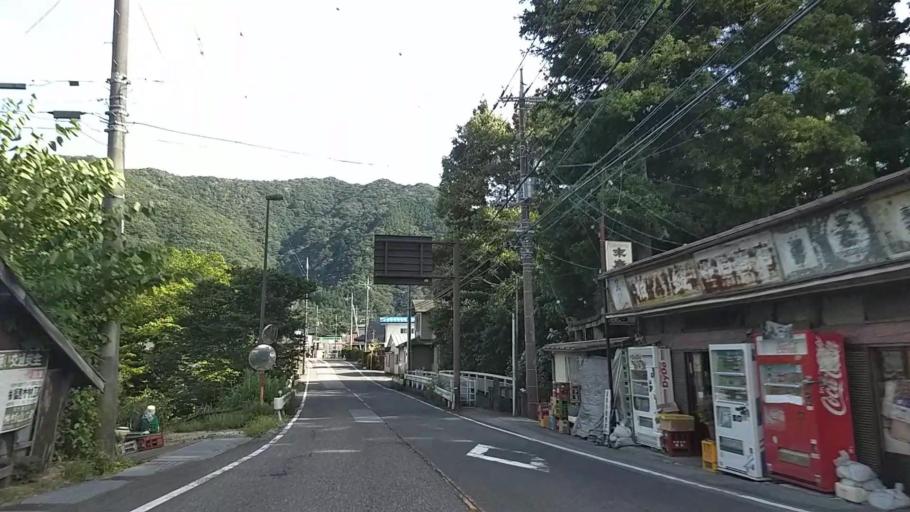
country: JP
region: Tochigi
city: Imaichi
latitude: 36.8555
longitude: 139.7299
